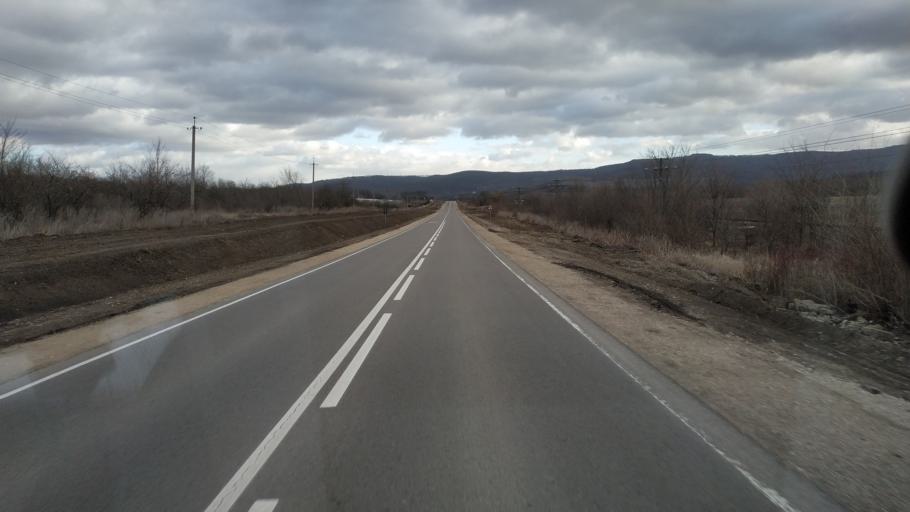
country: MD
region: Calarasi
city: Calarasi
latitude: 47.2641
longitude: 28.2337
